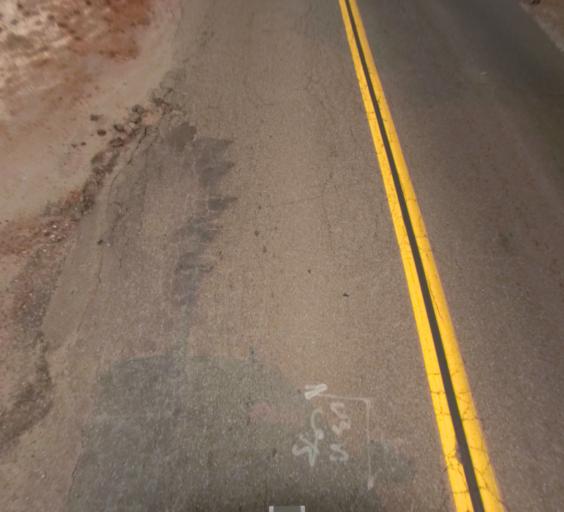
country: US
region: California
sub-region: Madera County
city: Oakhurst
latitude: 37.3365
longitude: -119.5832
